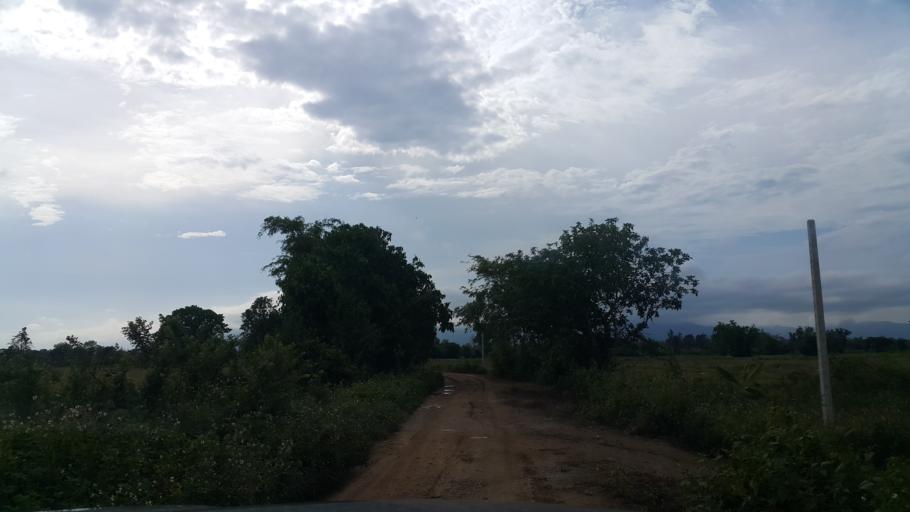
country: TH
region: Chiang Rai
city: Wiang Chai
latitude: 19.9731
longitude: 99.9163
